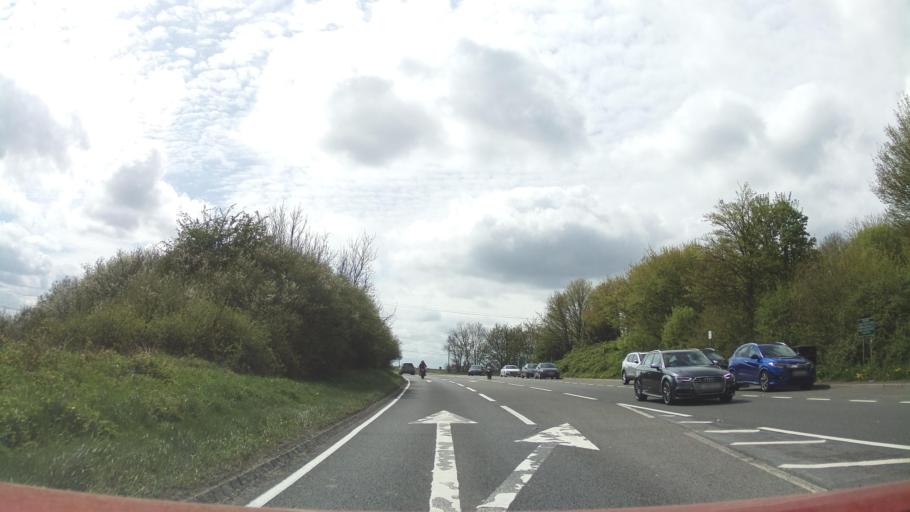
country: GB
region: England
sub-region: South Gloucestershire
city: Hinton
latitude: 51.4980
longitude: -2.3529
